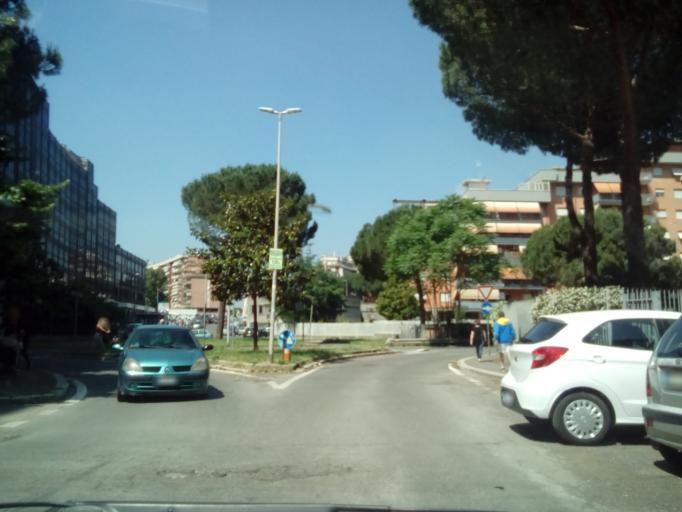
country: IT
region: Latium
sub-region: Citta metropolitana di Roma Capitale
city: Rome
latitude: 41.8832
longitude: 12.5900
